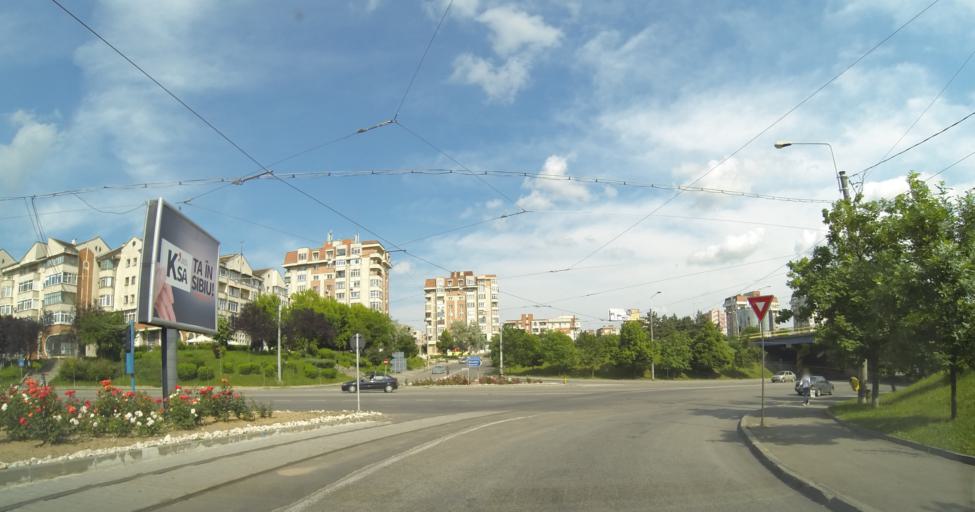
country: RO
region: Dolj
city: Craiova
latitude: 44.3143
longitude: 23.8342
